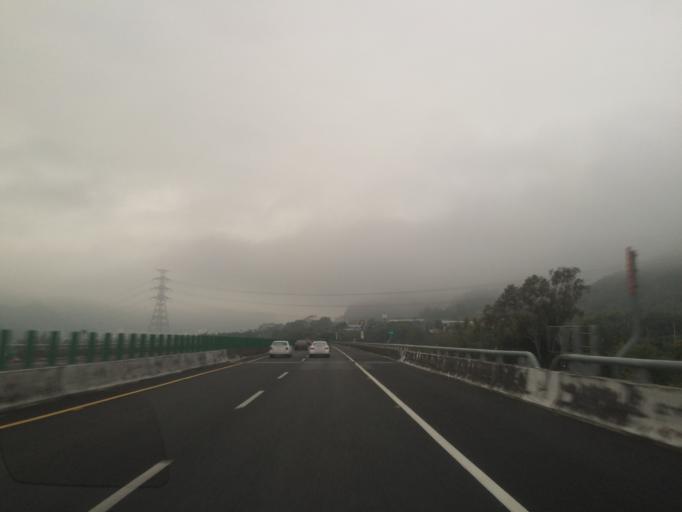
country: TW
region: Taiwan
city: Zhongxing New Village
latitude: 24.0001
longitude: 120.8049
